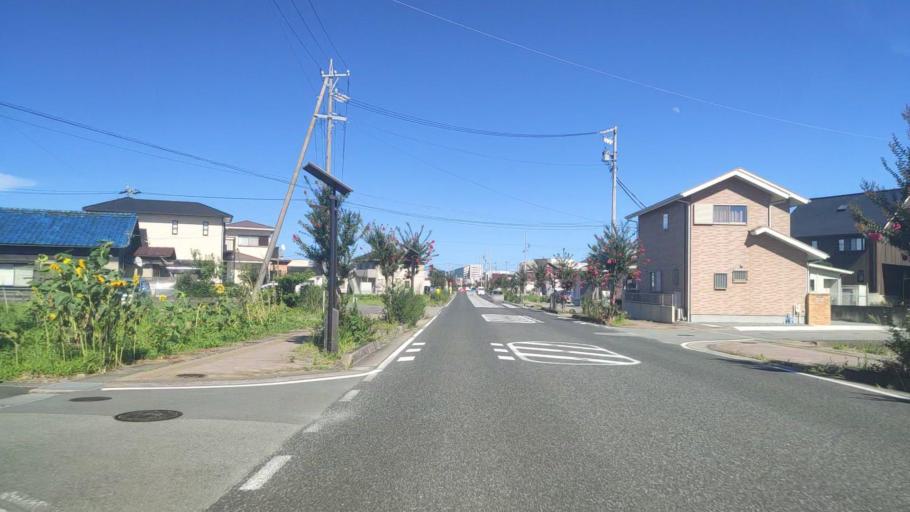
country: JP
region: Mie
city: Ise
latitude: 34.5001
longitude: 136.7045
